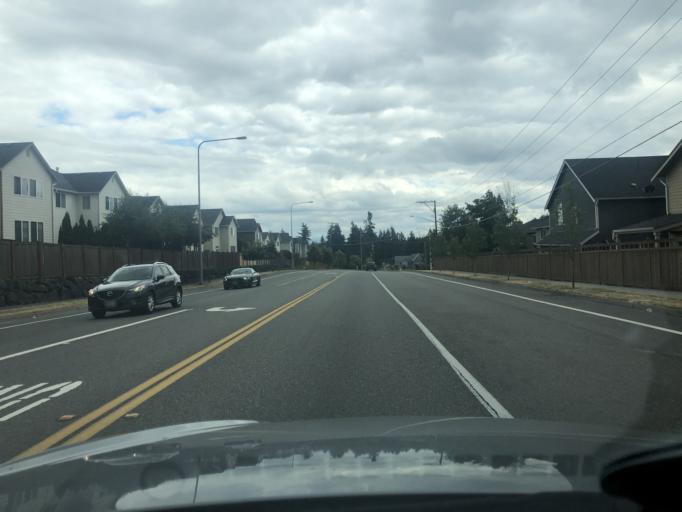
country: US
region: Washington
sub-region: King County
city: Lea Hill
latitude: 47.3252
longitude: -122.1658
